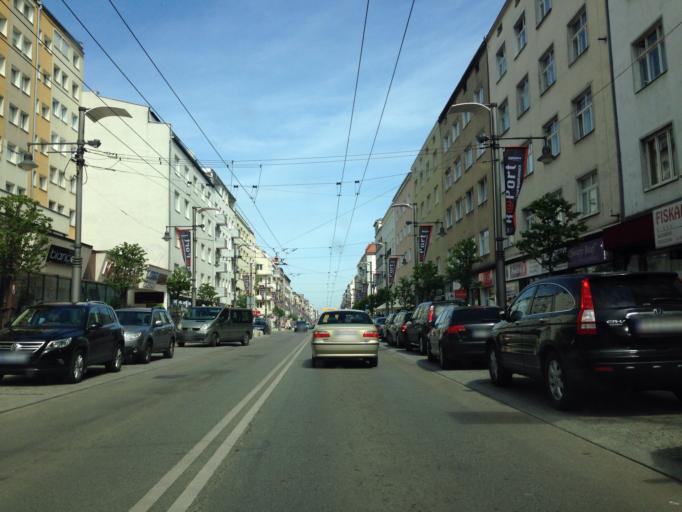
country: PL
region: Pomeranian Voivodeship
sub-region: Gdynia
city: Gdynia
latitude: 54.5103
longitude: 18.5386
